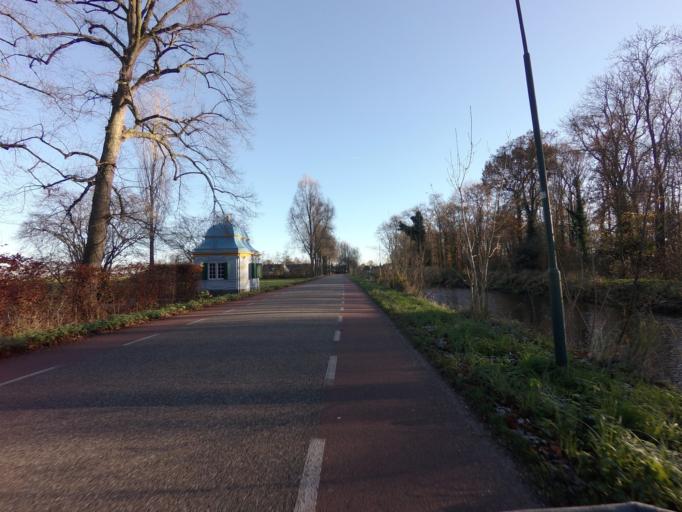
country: NL
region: Utrecht
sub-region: Stichtse Vecht
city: Vreeland
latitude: 52.2325
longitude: 4.9951
